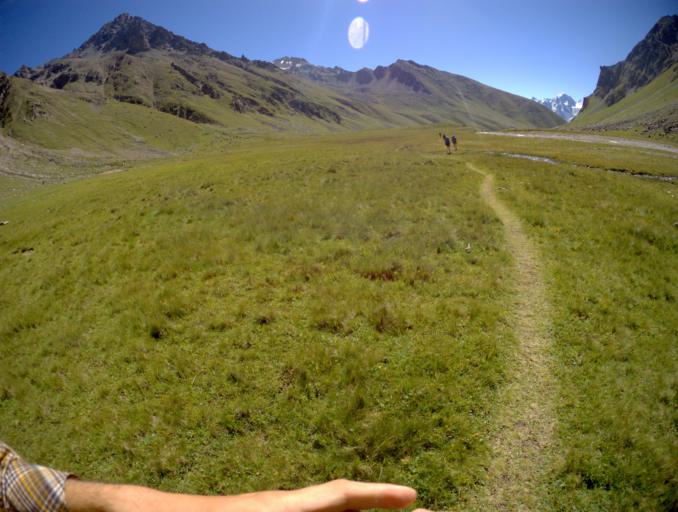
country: RU
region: Kabardino-Balkariya
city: Terskol
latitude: 43.3207
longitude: 42.5746
